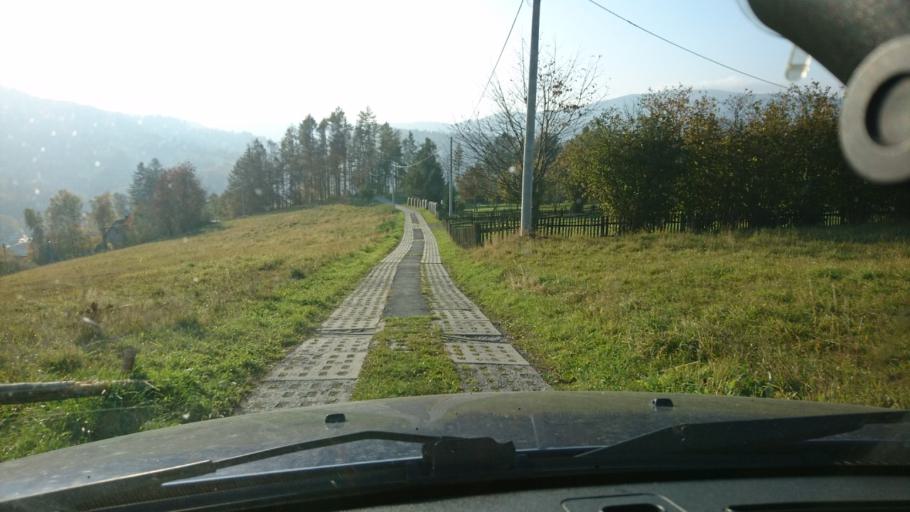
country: PL
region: Silesian Voivodeship
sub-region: Powiat cieszynski
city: Wisla
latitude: 49.6616
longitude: 18.8641
